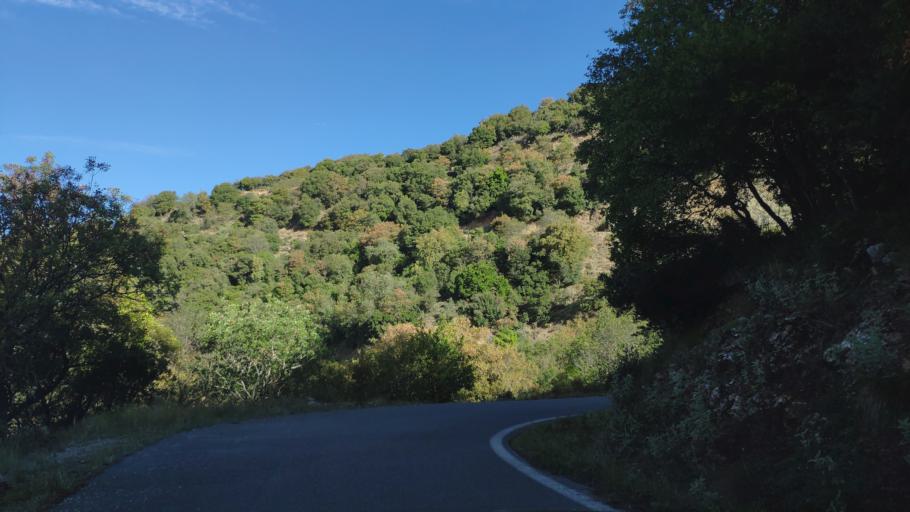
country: GR
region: Peloponnese
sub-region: Nomos Arkadias
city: Dimitsana
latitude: 37.5497
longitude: 22.0577
